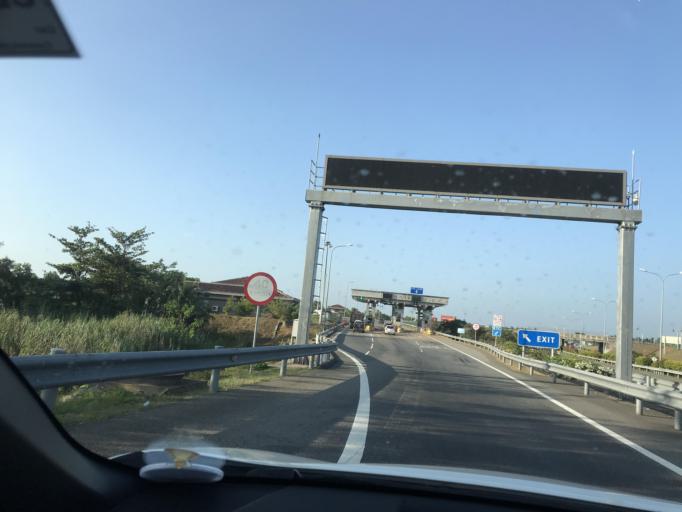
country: LK
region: Western
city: Ja Ela
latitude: 7.0793
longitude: 79.8773
